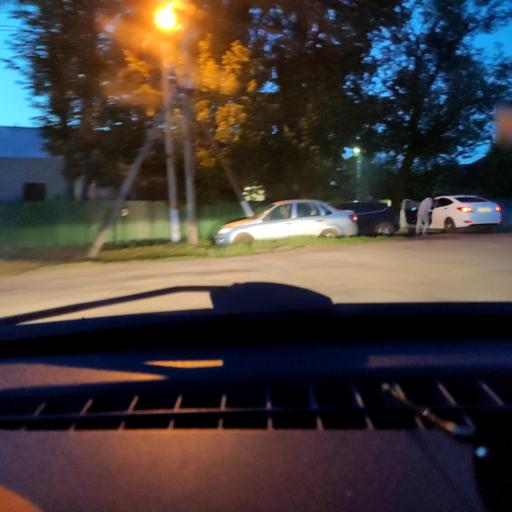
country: RU
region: Bashkortostan
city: Karmaskaly
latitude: 54.3707
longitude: 56.1655
